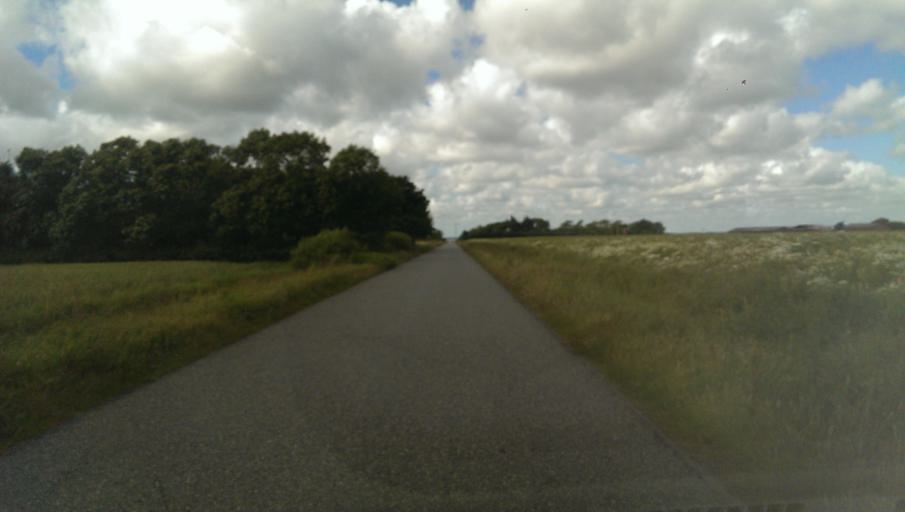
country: DK
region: Central Jutland
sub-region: Holstebro Kommune
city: Ulfborg
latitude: 56.2721
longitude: 8.2474
